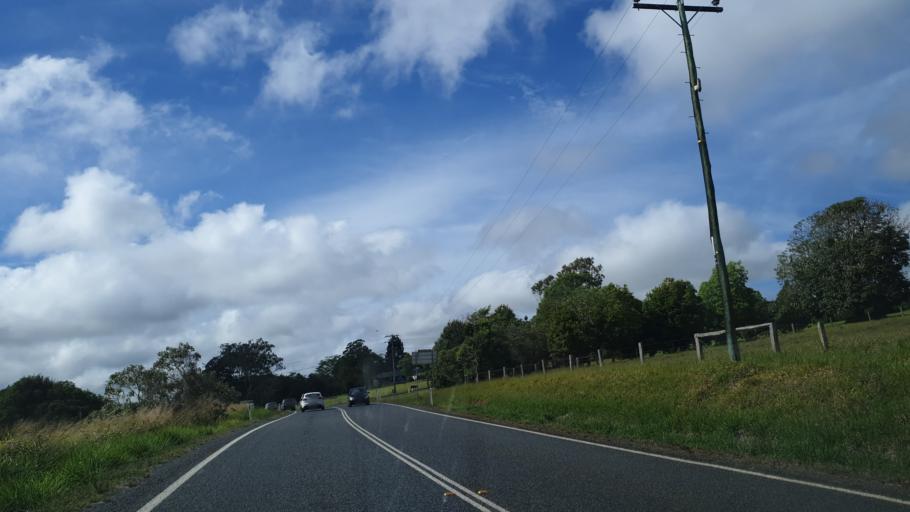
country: AU
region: Queensland
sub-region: Tablelands
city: Atherton
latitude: -17.3478
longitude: 145.5800
